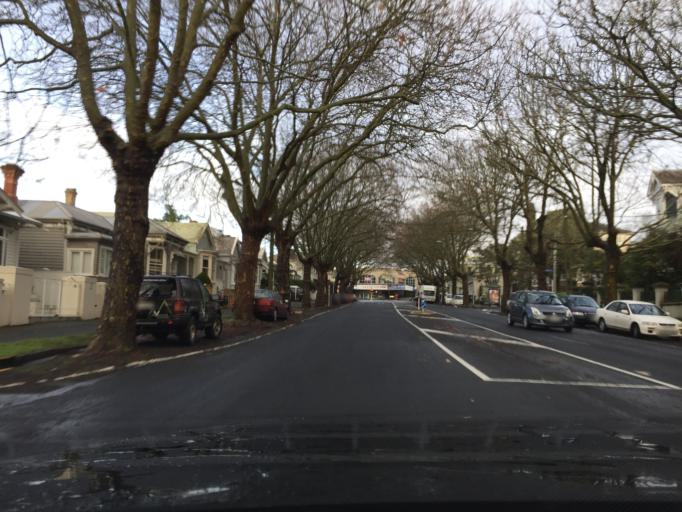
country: NZ
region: Auckland
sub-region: Auckland
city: Auckland
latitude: -36.8527
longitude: 174.7470
